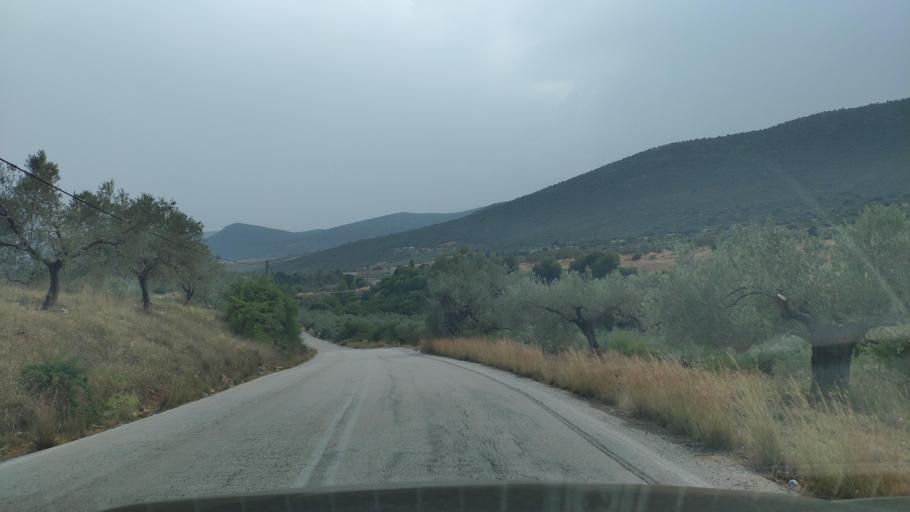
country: GR
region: Peloponnese
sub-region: Nomos Argolidos
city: Palaia Epidavros
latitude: 37.5745
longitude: 23.1502
